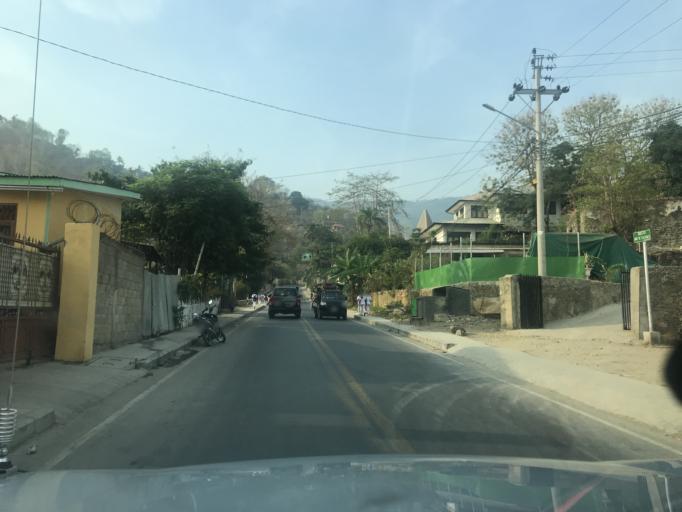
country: TL
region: Dili
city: Dili
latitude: -8.5725
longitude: 125.5828
